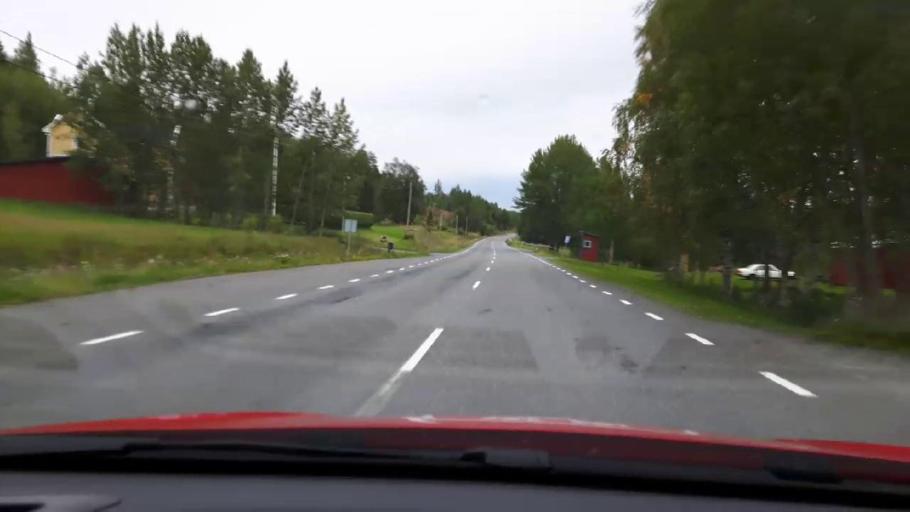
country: SE
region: Jaemtland
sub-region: Are Kommun
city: Jarpen
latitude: 63.3915
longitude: 13.3906
